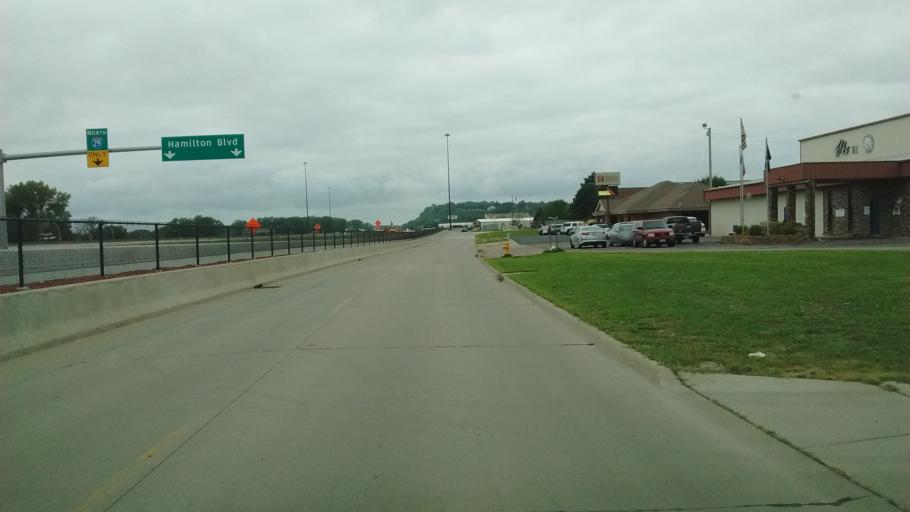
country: US
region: Iowa
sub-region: Woodbury County
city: Sioux City
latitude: 42.4925
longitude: -96.4163
